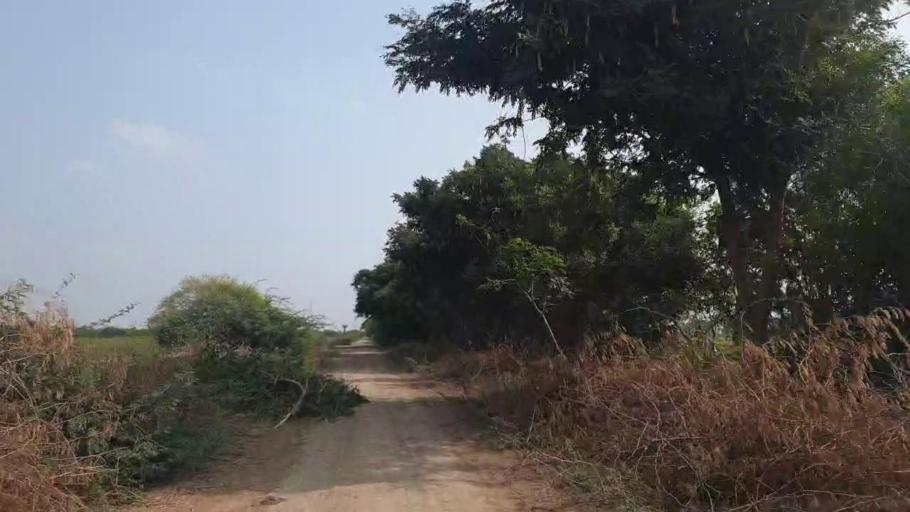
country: PK
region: Sindh
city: Badin
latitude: 24.5476
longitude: 68.7107
